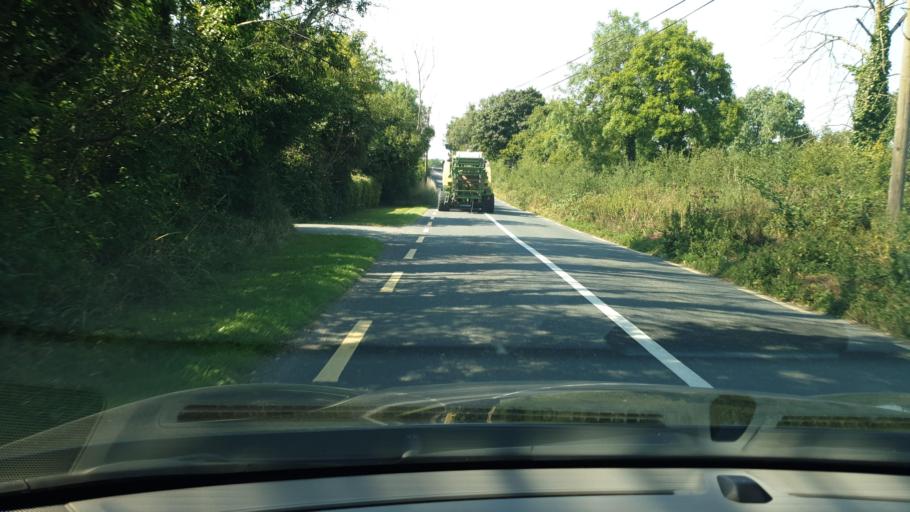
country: IE
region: Leinster
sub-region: An Mhi
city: Athboy
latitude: 53.6048
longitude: -6.8863
